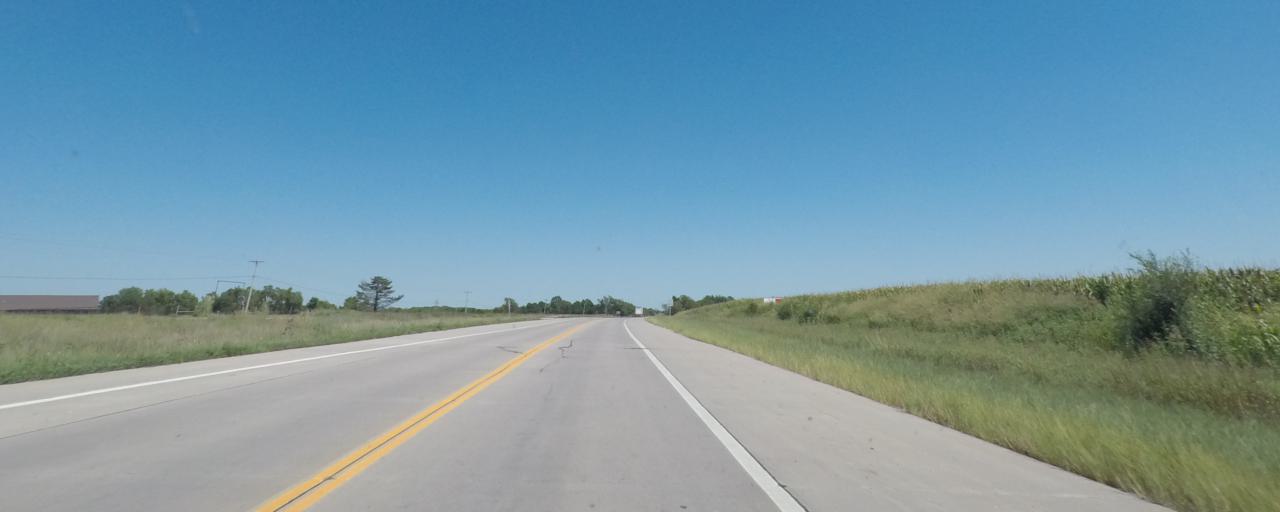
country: US
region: Kansas
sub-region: Lyon County
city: Emporia
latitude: 38.4121
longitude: -96.2797
